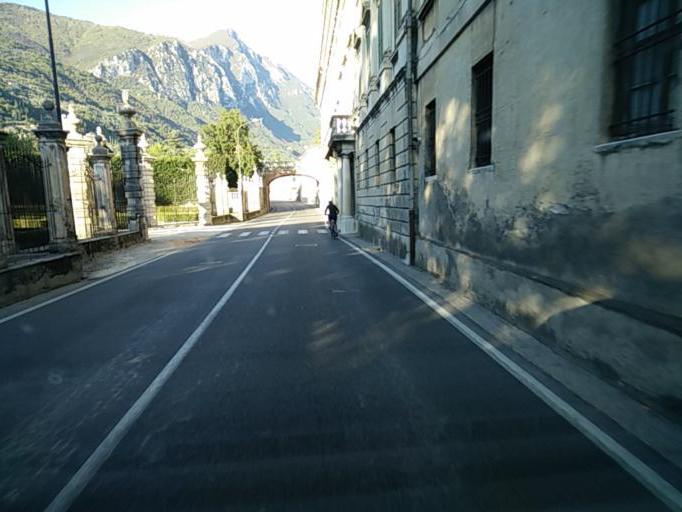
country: IT
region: Lombardy
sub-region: Provincia di Brescia
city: Gargnano
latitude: 45.6769
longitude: 10.6528
